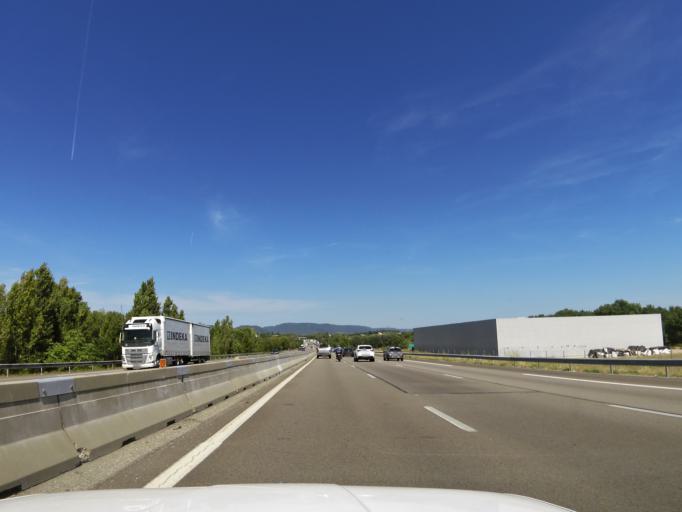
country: FR
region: Rhone-Alpes
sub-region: Departement de la Drome
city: Montboucher-sur-Jabron
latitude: 44.5380
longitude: 4.8049
